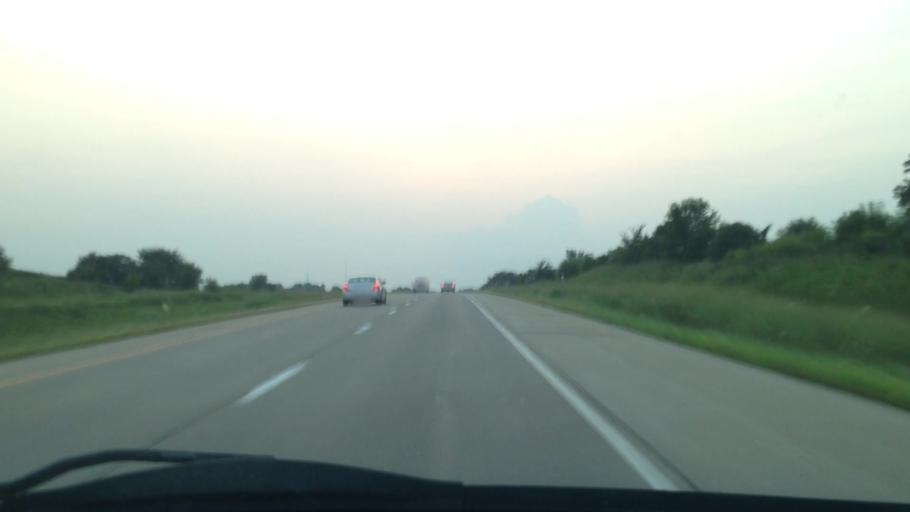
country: US
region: Iowa
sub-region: Buchanan County
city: Jesup
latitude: 42.3397
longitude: -92.0264
